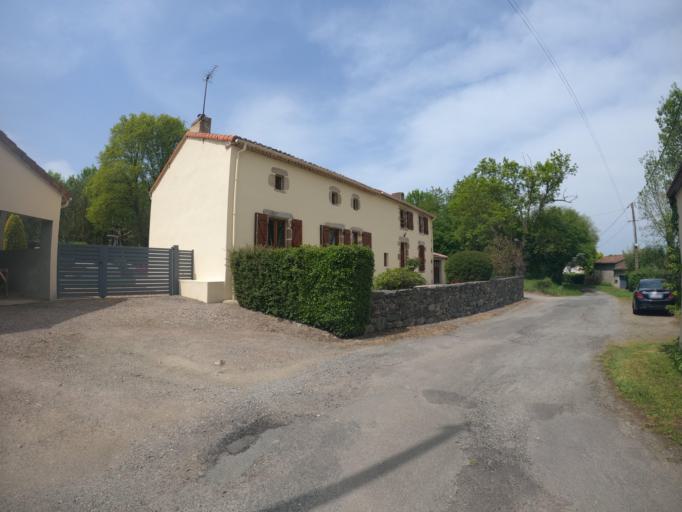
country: FR
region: Poitou-Charentes
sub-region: Departement des Deux-Sevres
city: La Chapelle-Saint-Laurent
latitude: 46.7611
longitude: -0.4659
